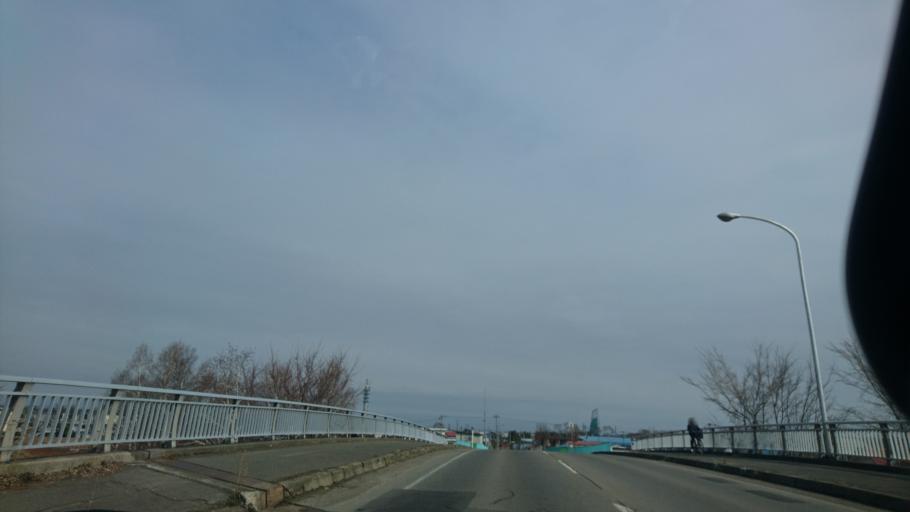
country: JP
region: Hokkaido
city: Obihiro
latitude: 42.9489
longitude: 143.2075
